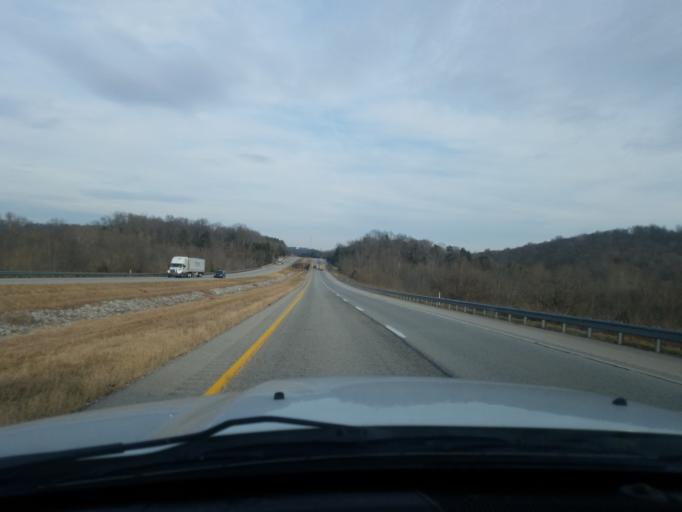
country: US
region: Indiana
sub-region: Harrison County
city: Corydon
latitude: 38.2350
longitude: -86.2310
